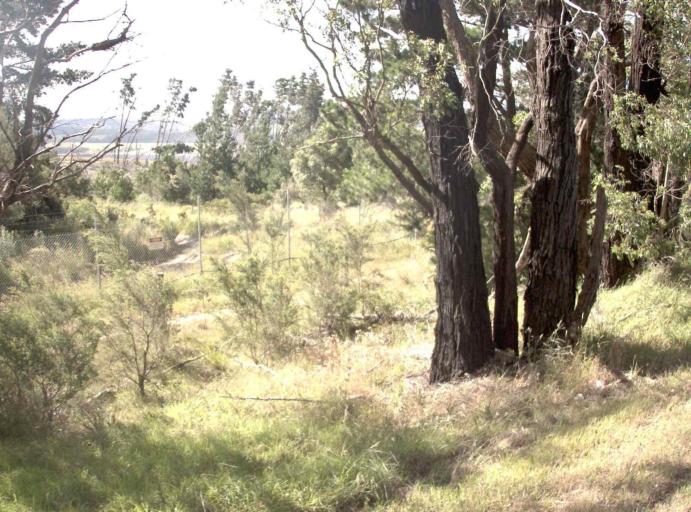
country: AU
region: Victoria
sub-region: Latrobe
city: Morwell
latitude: -38.1896
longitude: 146.4041
